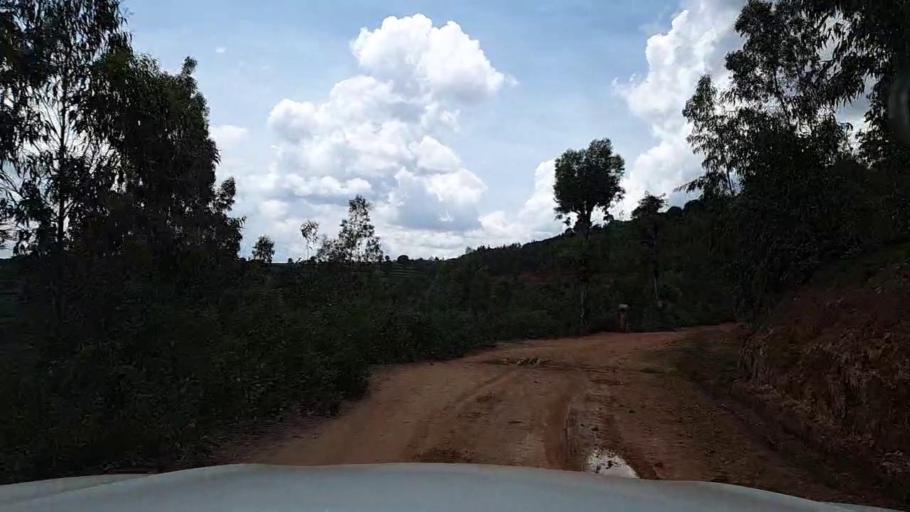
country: RW
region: Southern Province
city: Butare
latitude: -2.7555
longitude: 29.7523
